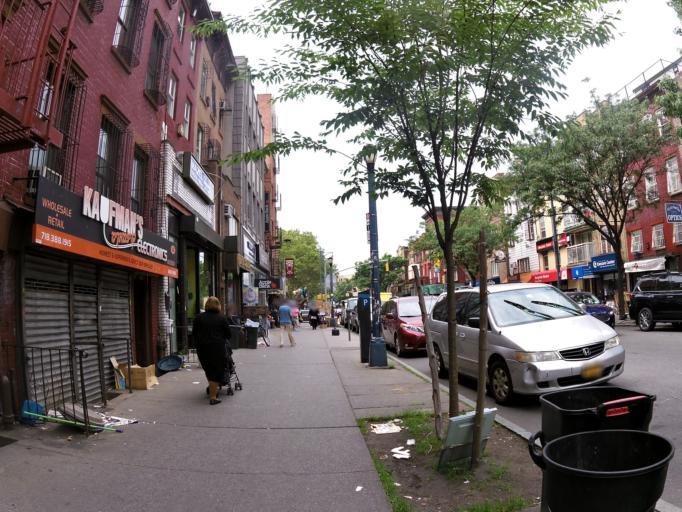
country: US
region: New York
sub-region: Queens County
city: Long Island City
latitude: 40.7059
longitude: -73.9603
